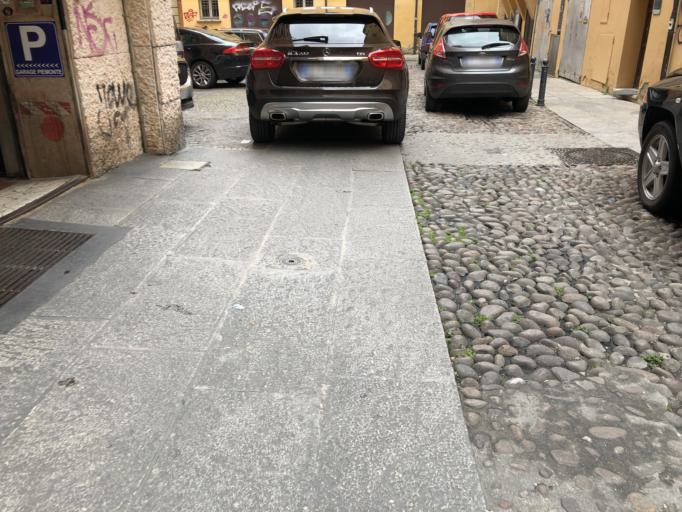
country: IT
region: Emilia-Romagna
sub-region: Provincia di Bologna
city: Bologna
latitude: 44.4957
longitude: 11.3478
